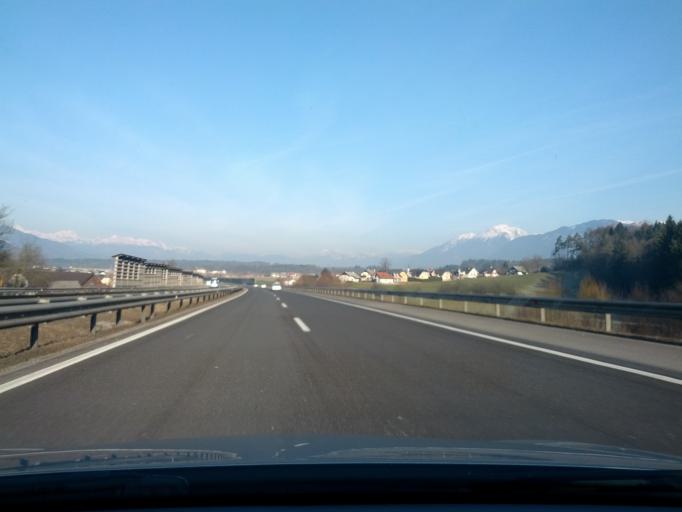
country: SI
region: Naklo
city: Naklo
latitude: 46.2726
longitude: 14.3257
